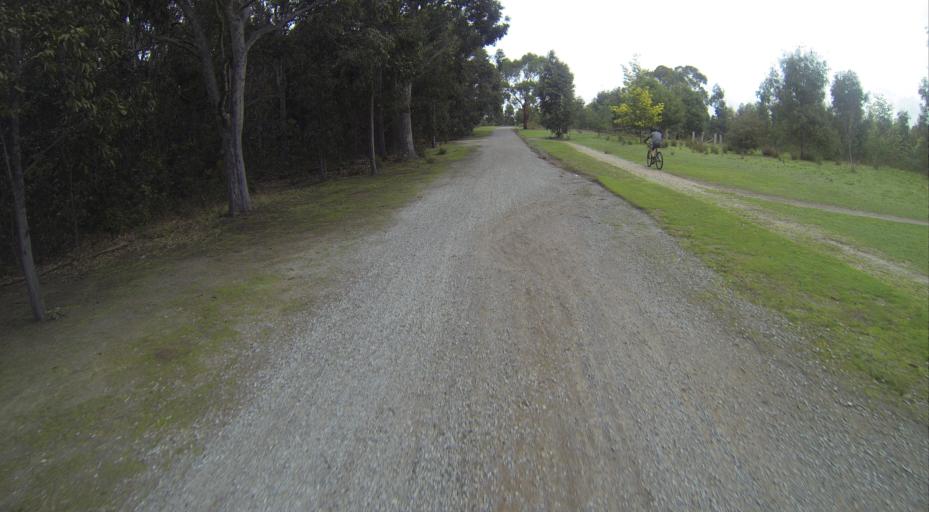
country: AU
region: Victoria
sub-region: Yarra Ranges
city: Lysterfield
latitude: -37.9519
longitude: 145.2822
